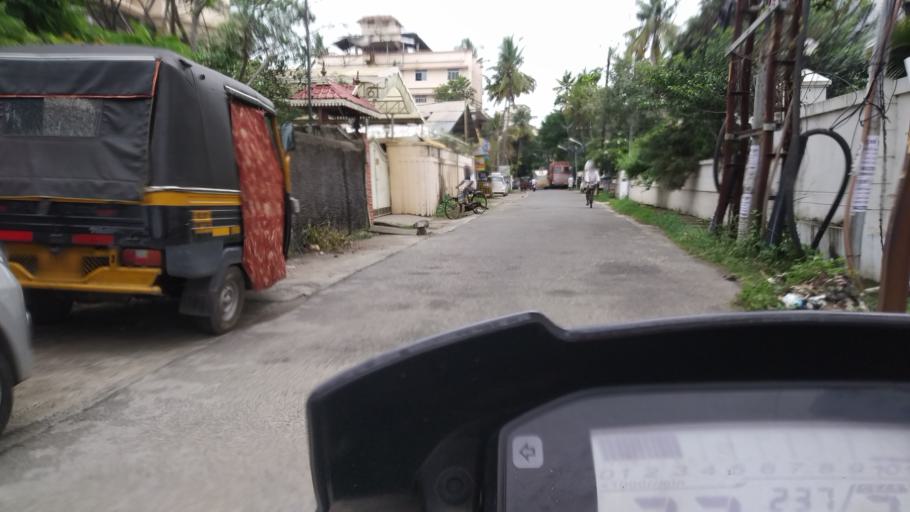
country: IN
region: Kerala
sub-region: Ernakulam
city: Cochin
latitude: 9.9927
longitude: 76.2840
